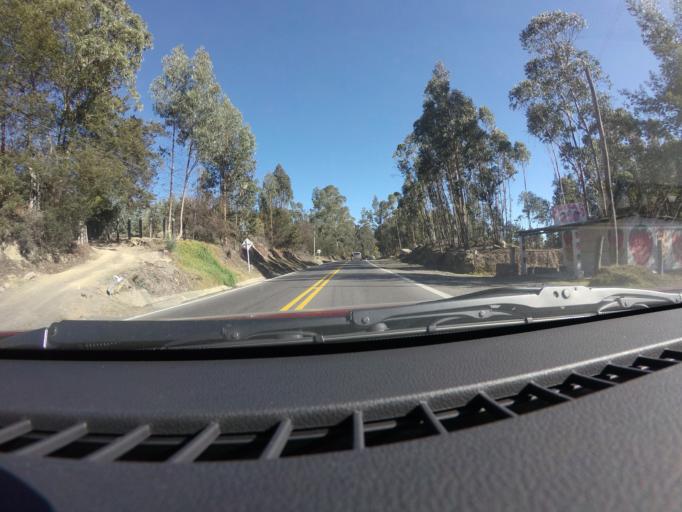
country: CO
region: Cundinamarca
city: Sutatausa
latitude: 5.2631
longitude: -73.8465
